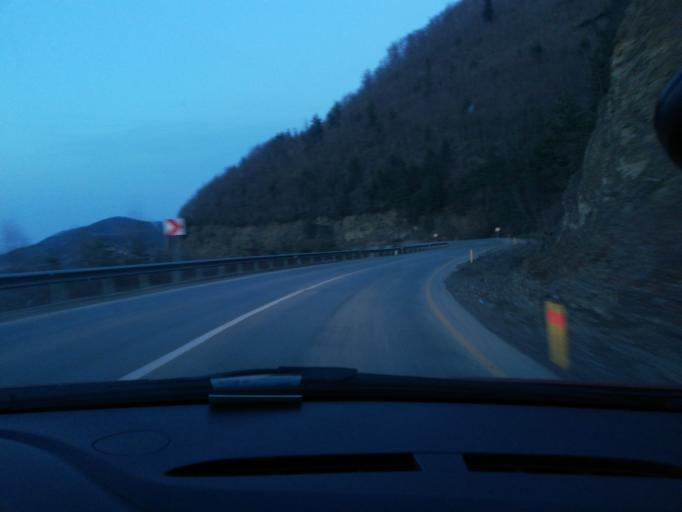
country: TR
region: Kastamonu
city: Inebolu
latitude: 41.9211
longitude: 33.7350
